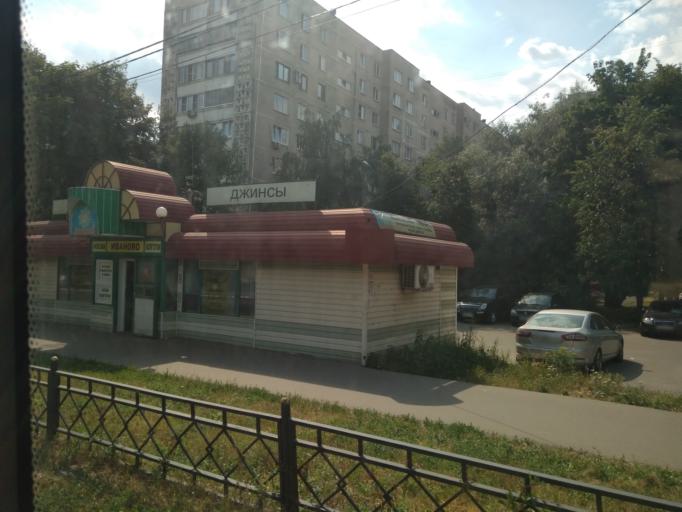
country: RU
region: Moskovskaya
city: Bykovo
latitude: 55.6069
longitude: 38.0752
